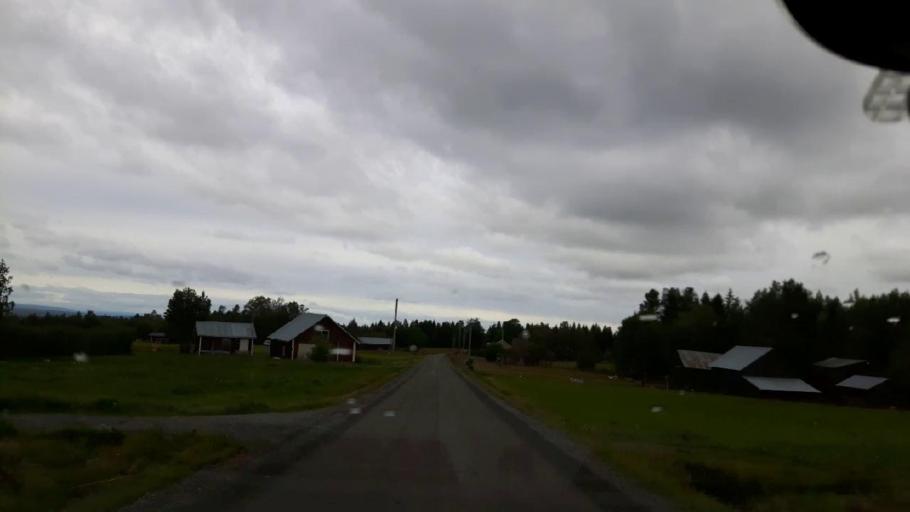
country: SE
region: Jaemtland
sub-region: OEstersunds Kommun
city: Ostersund
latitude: 63.0559
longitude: 14.5609
